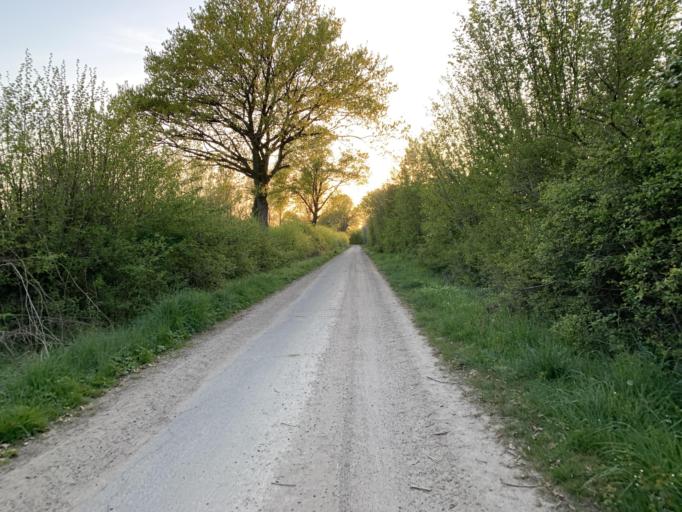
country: DE
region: Schleswig-Holstein
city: Worth
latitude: 53.4685
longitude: 10.4207
